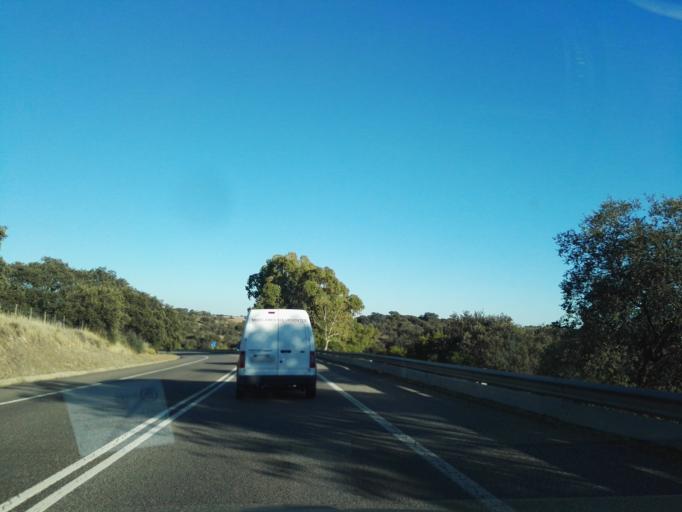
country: PT
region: Evora
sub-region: Vila Vicosa
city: Vila Vicosa
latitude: 38.8453
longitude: -7.3780
